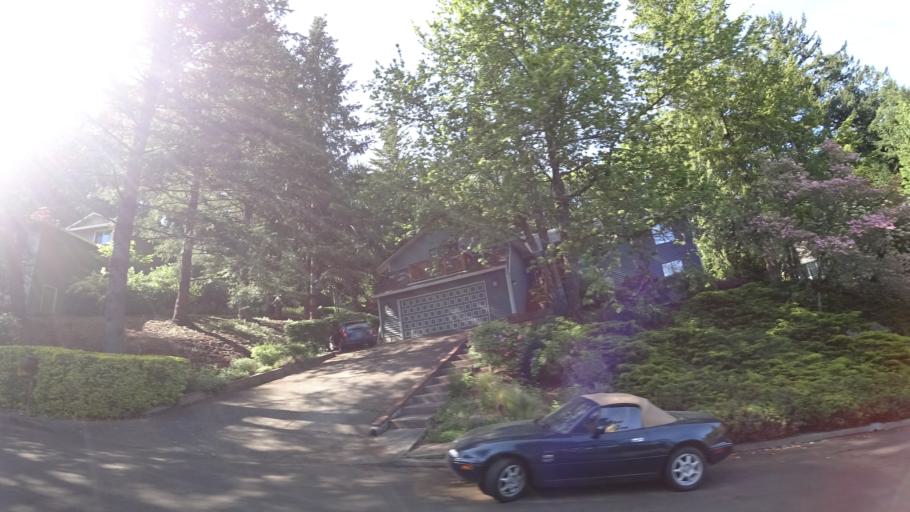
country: US
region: Oregon
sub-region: Washington County
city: West Slope
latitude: 45.4994
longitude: -122.7464
